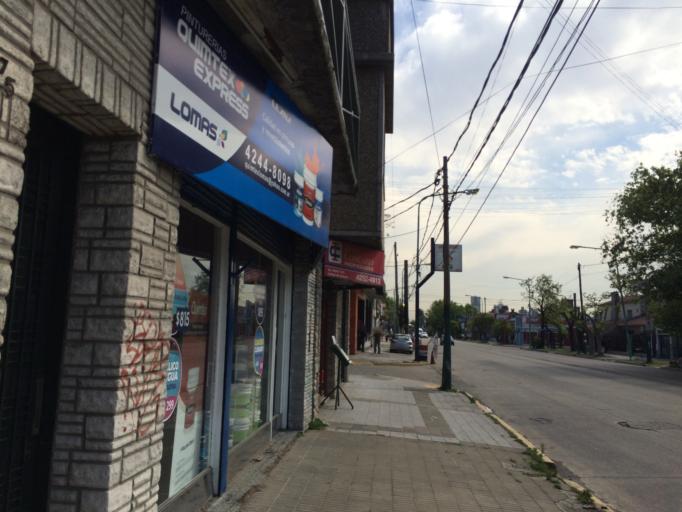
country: AR
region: Buenos Aires
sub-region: Partido de Lomas de Zamora
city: Lomas de Zamora
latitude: -34.7538
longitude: -58.3953
